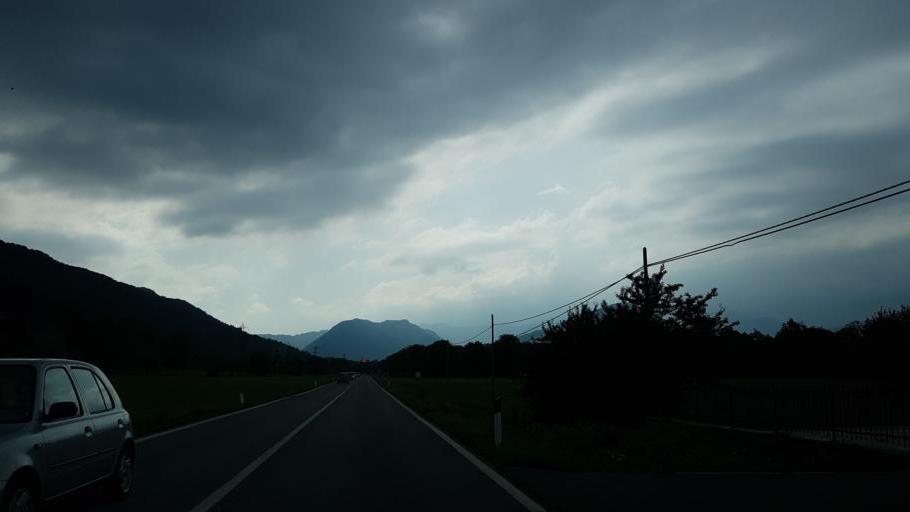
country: IT
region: Piedmont
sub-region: Provincia di Cuneo
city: Roccasparvera
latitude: 44.3338
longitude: 7.4474
